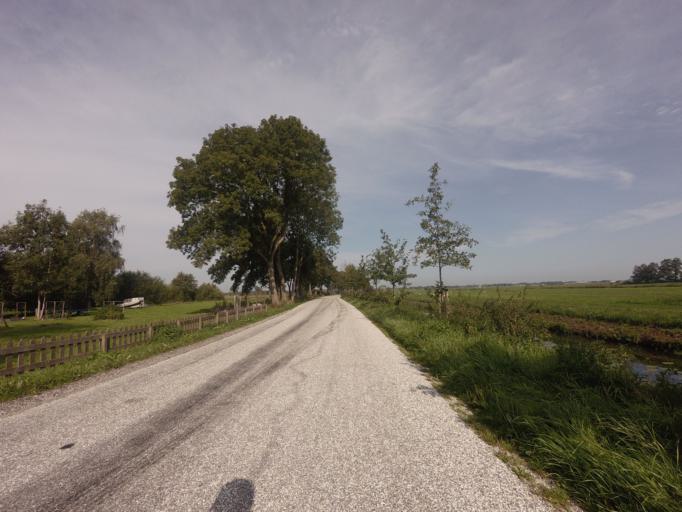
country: NL
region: Groningen
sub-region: Gemeente Leek
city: Leek
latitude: 53.2022
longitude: 6.3497
